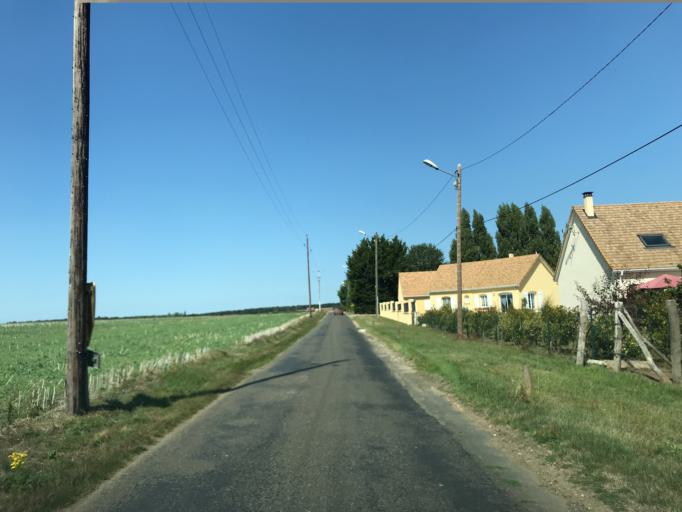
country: FR
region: Haute-Normandie
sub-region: Departement de l'Eure
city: Houlbec-Cocherel
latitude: 49.0612
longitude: 1.2701
